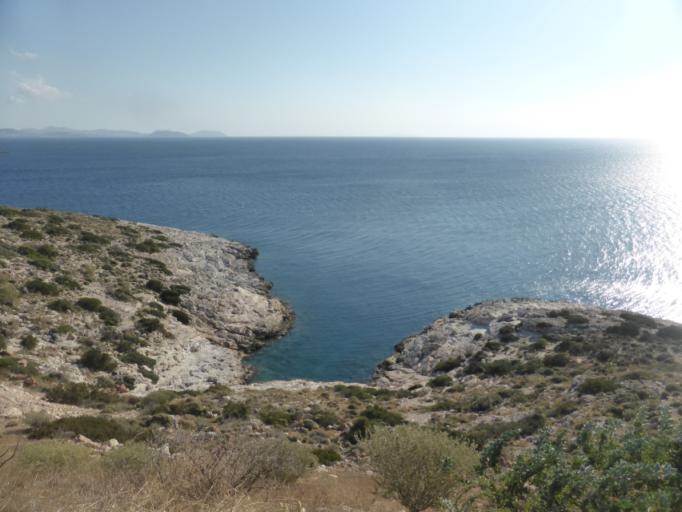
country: GR
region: Attica
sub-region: Nomarchia Anatolikis Attikis
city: Vouliagmeni
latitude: 37.8013
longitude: 23.7942
